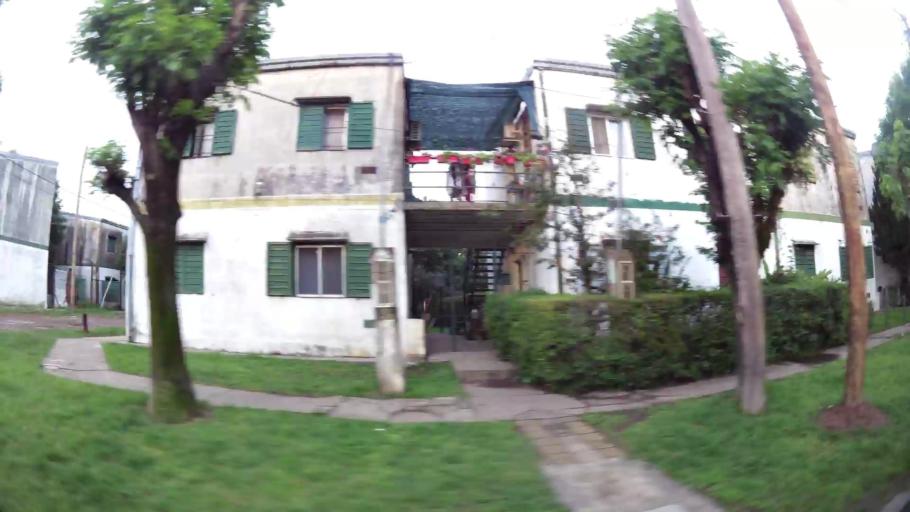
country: AR
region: Buenos Aires
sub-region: Partido de Almirante Brown
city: Adrogue
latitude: -34.7583
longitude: -58.3412
